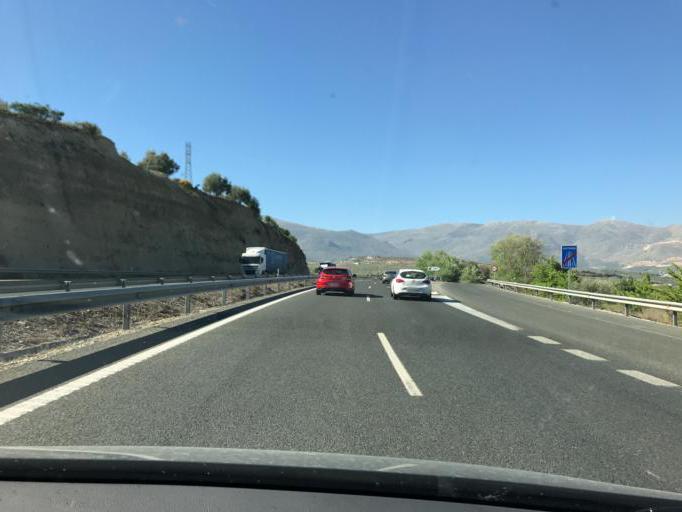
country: ES
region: Andalusia
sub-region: Provincia de Granada
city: Salar
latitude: 37.1723
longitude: -4.0828
